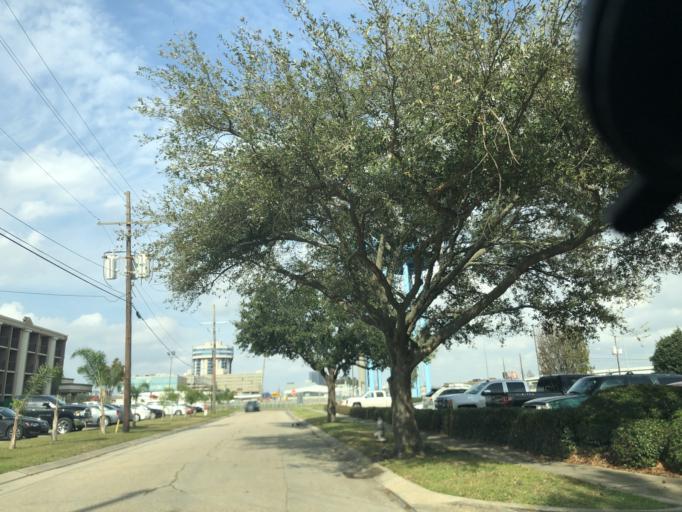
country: US
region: Louisiana
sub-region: Jefferson Parish
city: Metairie
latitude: 29.9955
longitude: -90.1585
